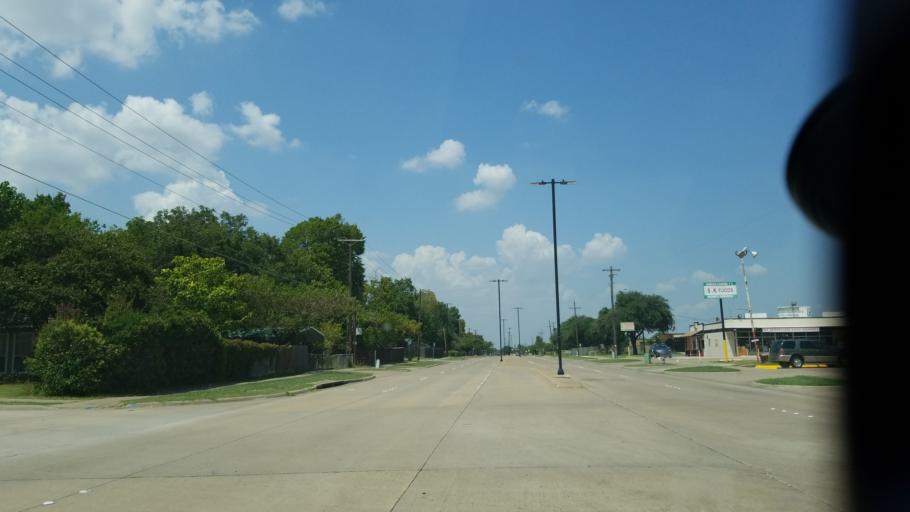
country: US
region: Texas
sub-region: Dallas County
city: Garland
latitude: 32.9240
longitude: -96.6395
